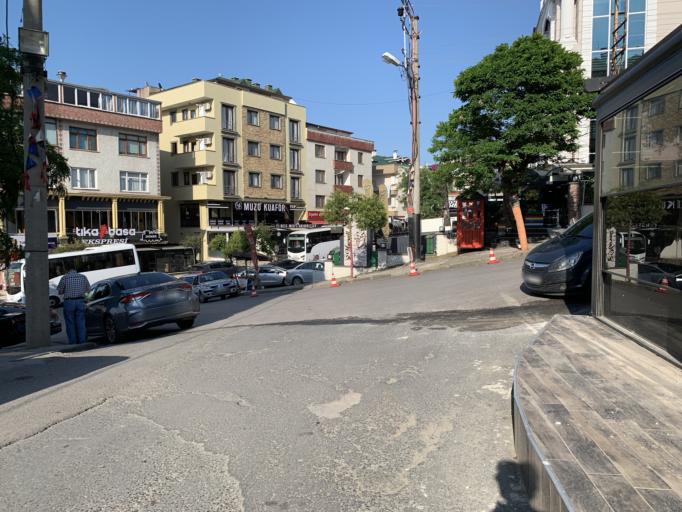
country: TR
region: Trabzon
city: Trabzon
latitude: 40.9964
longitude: 39.7619
